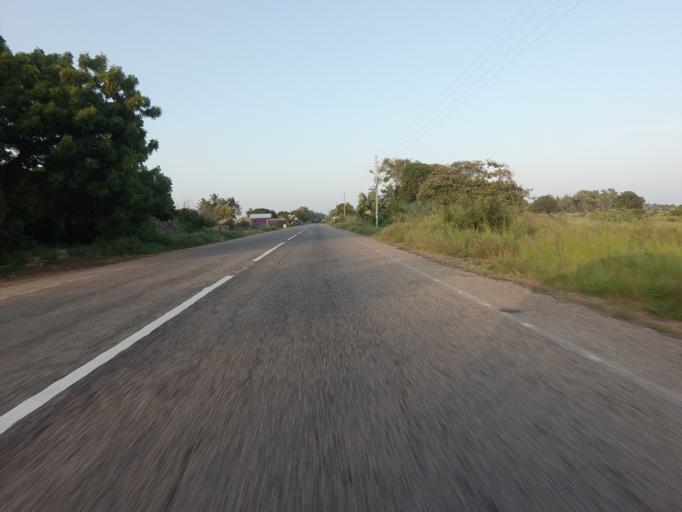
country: GH
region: Volta
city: Anloga
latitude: 5.7894
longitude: 0.8648
